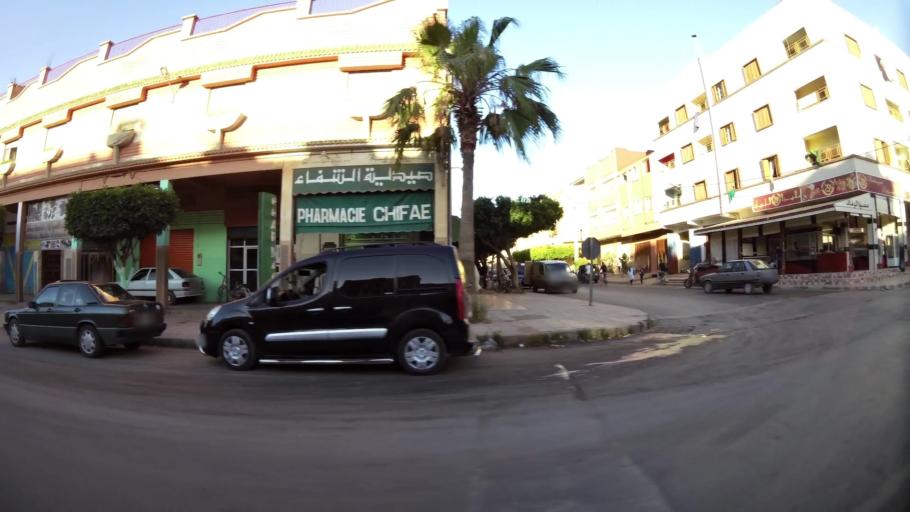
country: MA
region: Oriental
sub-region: Berkane-Taourirt
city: Berkane
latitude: 34.9246
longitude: -2.3180
